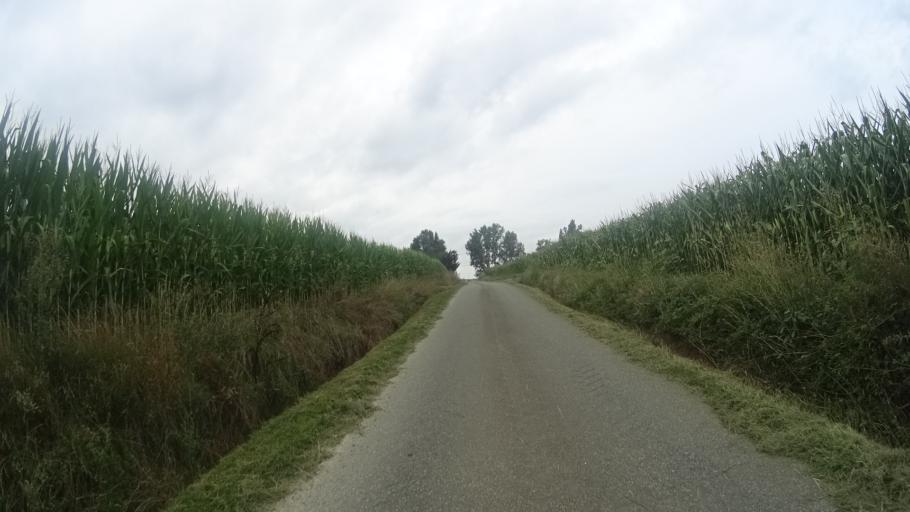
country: FR
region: Aquitaine
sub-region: Departement des Pyrenees-Atlantiques
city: Orthez
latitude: 43.4859
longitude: -0.7080
